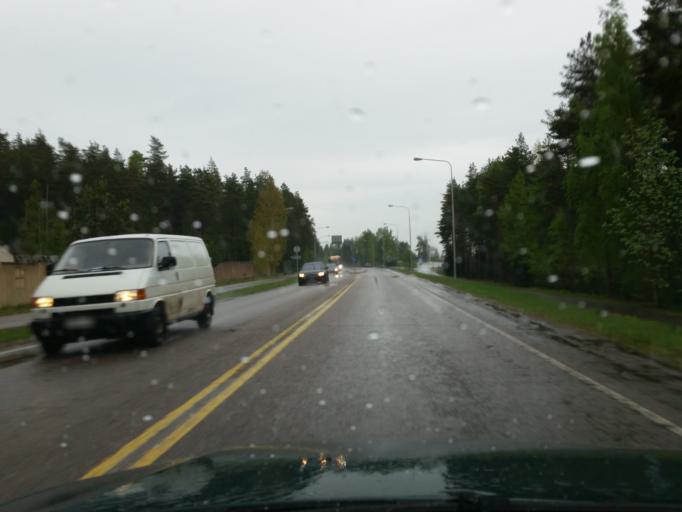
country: FI
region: Uusimaa
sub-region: Helsinki
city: Lohja
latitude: 60.2787
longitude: 24.1480
